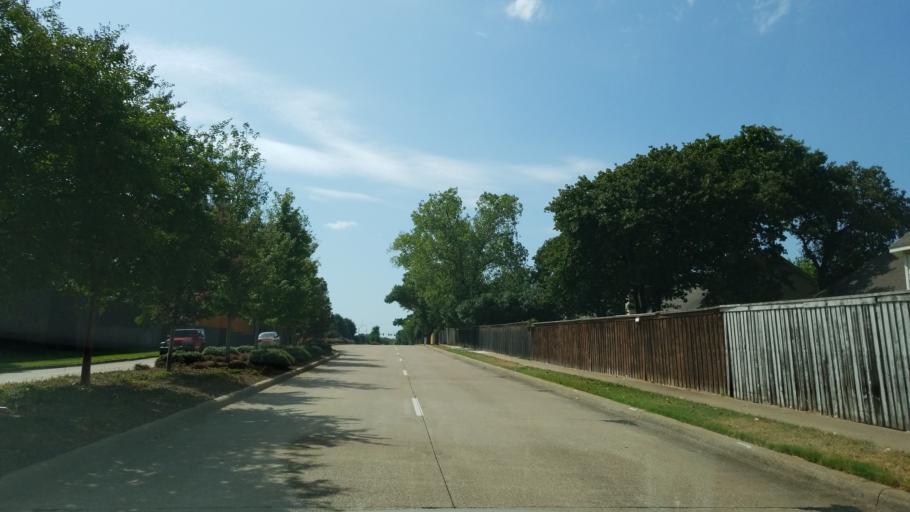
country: US
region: Texas
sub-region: Tarrant County
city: Euless
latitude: 32.8845
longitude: -97.0910
